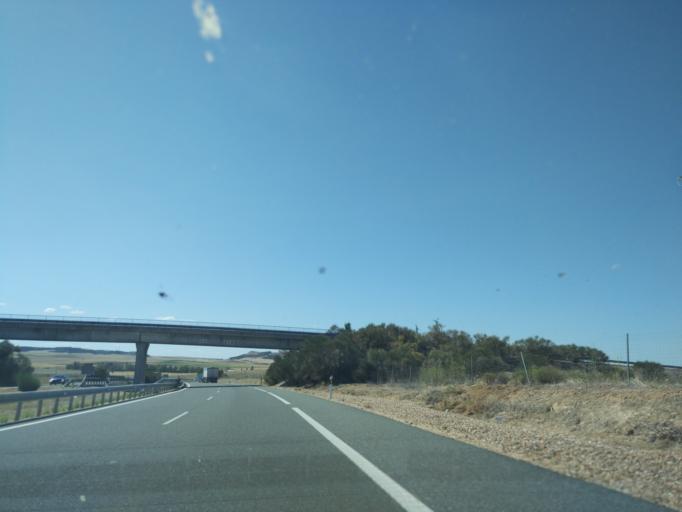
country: ES
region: Castille and Leon
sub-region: Provincia de Valladolid
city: Vega de Valdetronco
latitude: 41.5817
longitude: -5.1054
